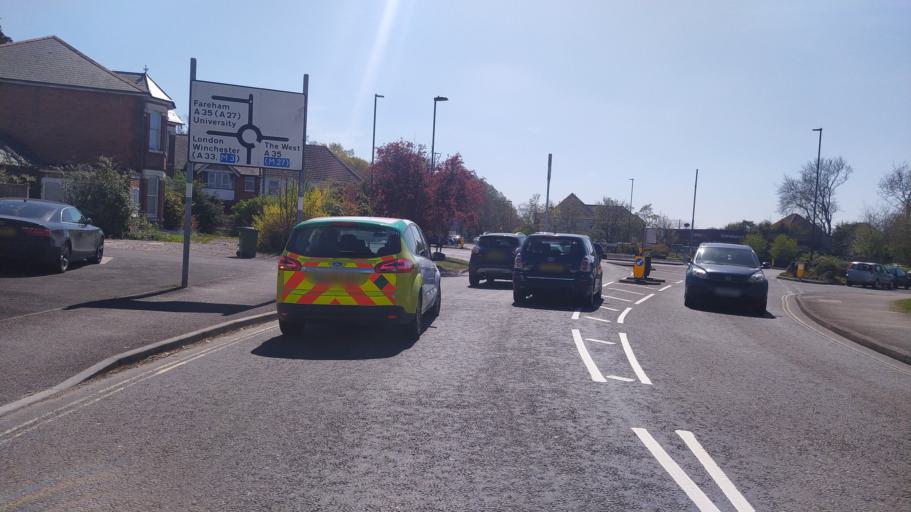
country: GB
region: England
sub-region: Southampton
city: Southampton
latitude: 50.9349
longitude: -1.4191
